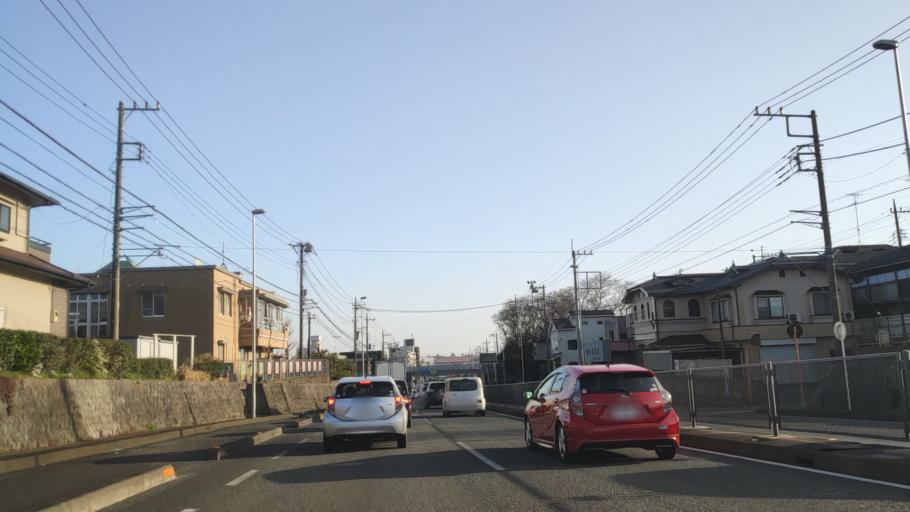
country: JP
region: Kanagawa
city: Zama
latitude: 35.4679
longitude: 139.3683
